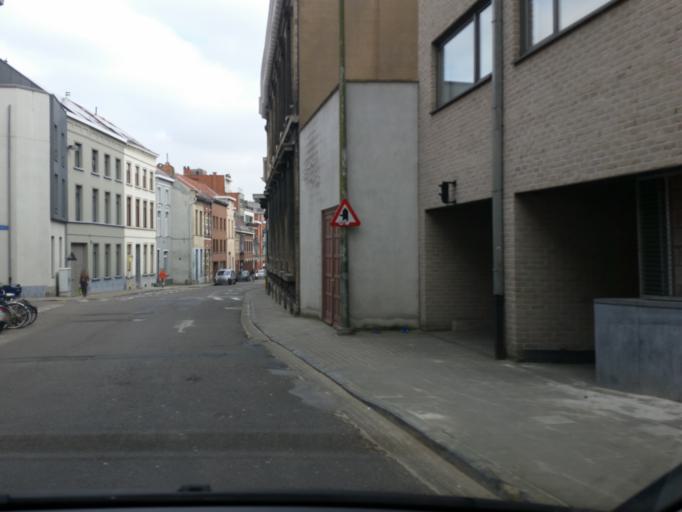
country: BE
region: Flanders
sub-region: Provincie Vlaams-Brabant
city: Leuven
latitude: 50.8820
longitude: 4.6883
